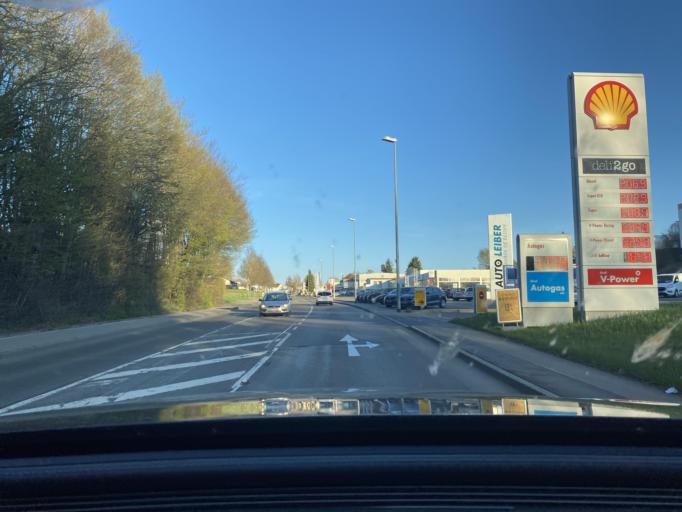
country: DE
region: Baden-Wuerttemberg
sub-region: Freiburg Region
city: Trossingen
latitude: 48.0771
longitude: 8.6219
